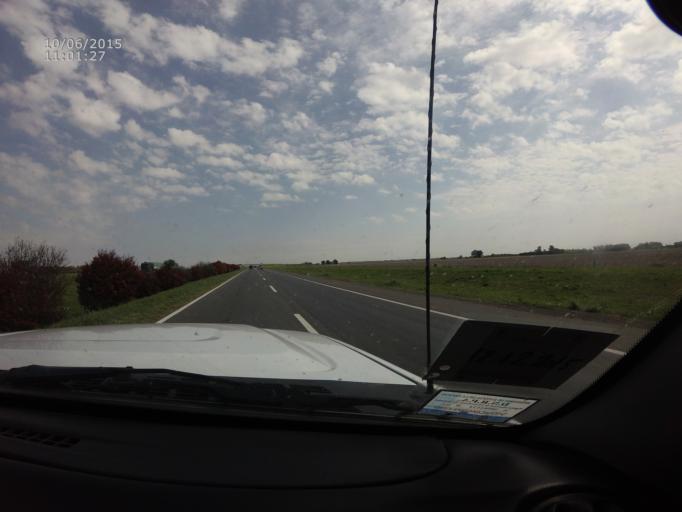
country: AR
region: Santa Fe
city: Villa Constitucion
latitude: -33.2595
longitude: -60.4158
